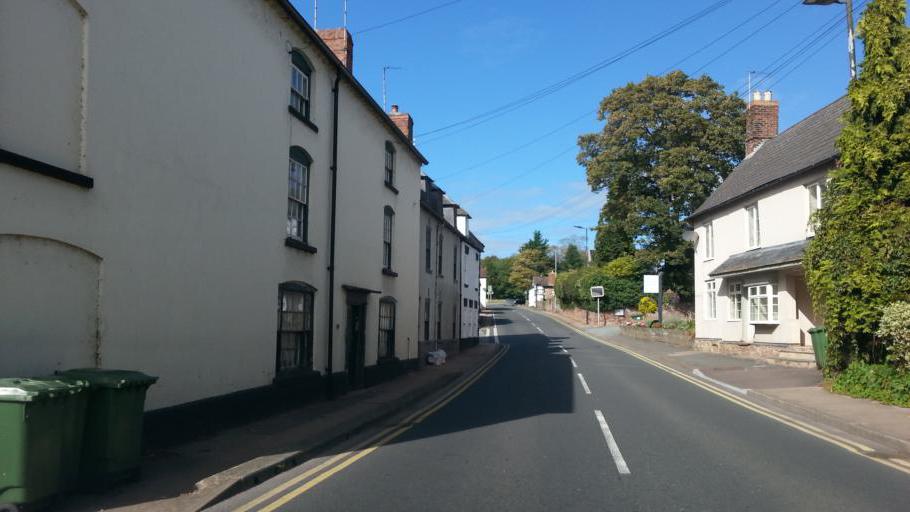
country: GB
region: England
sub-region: Herefordshire
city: Ross on Wye
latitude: 51.9151
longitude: -2.5981
